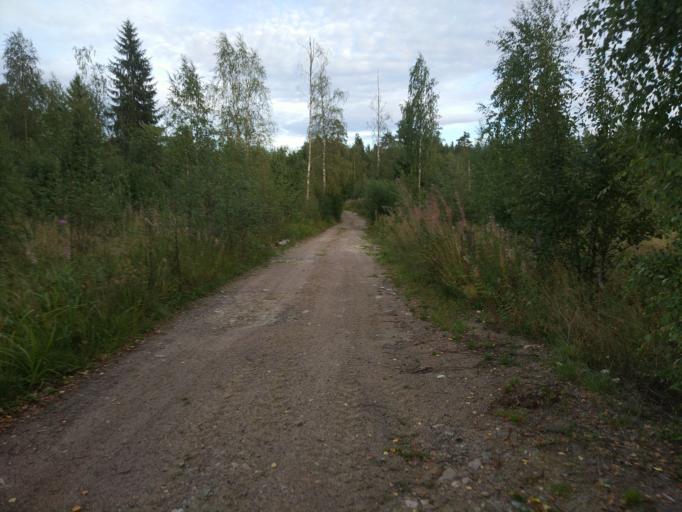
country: RU
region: Leningrad
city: Kuznechnoye
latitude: 61.1169
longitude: 29.6021
